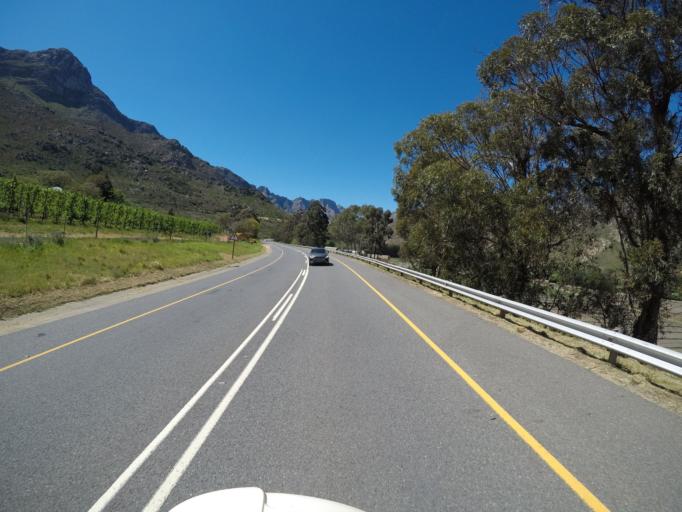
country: ZA
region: Western Cape
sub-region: Cape Winelands District Municipality
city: Ceres
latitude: -33.4206
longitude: 19.2538
